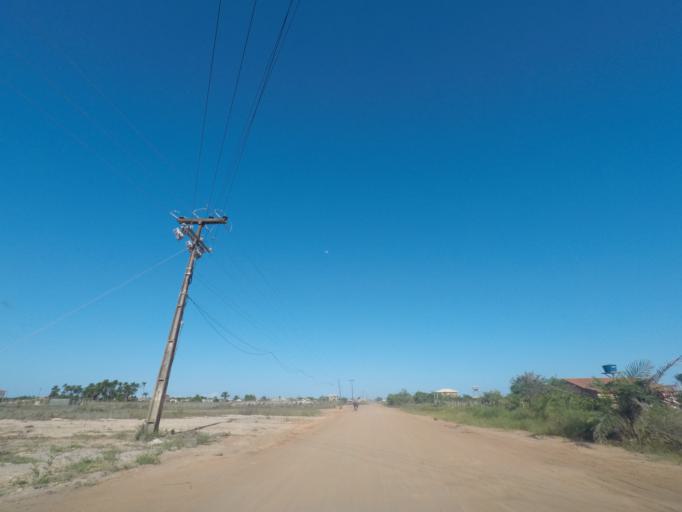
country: BR
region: Bahia
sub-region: Camamu
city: Camamu
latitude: -13.9329
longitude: -38.9467
